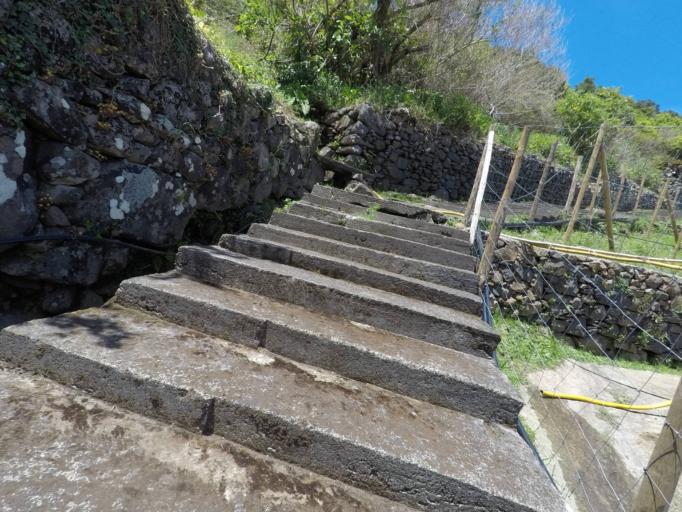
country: PT
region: Madeira
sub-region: Sao Vicente
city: Sao Vicente
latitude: 32.8227
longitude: -16.9784
